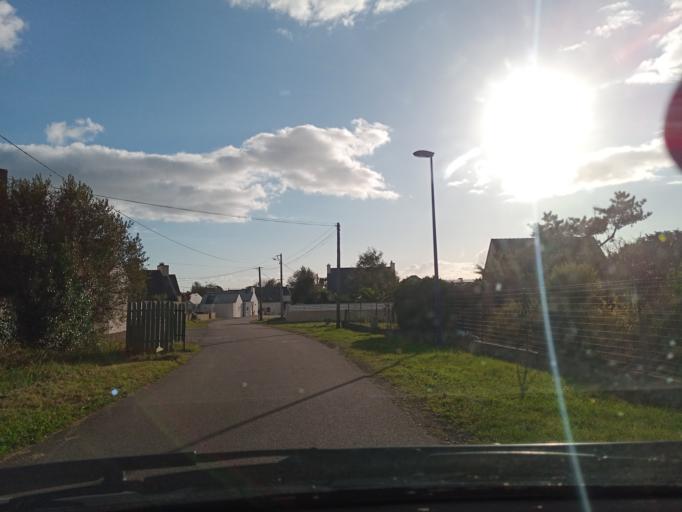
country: FR
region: Brittany
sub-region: Departement du Finistere
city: Audierne
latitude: 48.0202
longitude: -4.5142
